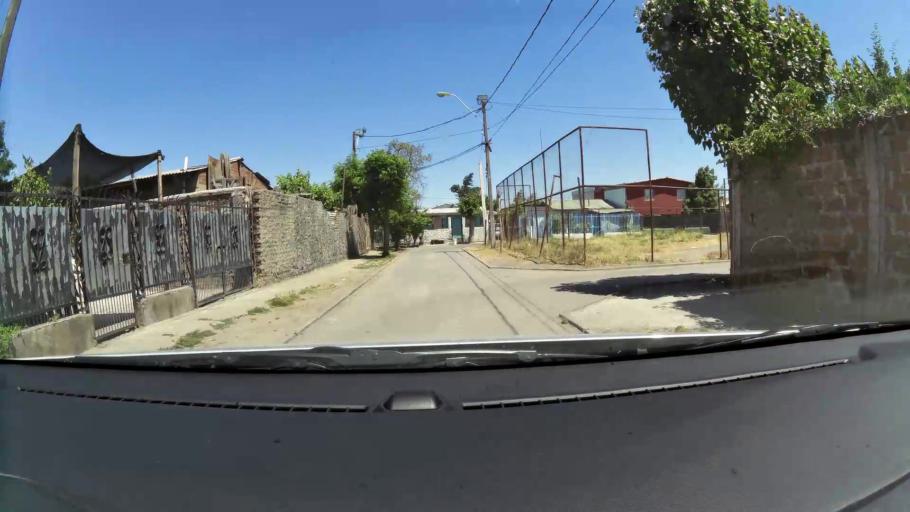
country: CL
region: Santiago Metropolitan
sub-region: Provincia de Santiago
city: La Pintana
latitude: -33.5685
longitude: -70.6655
